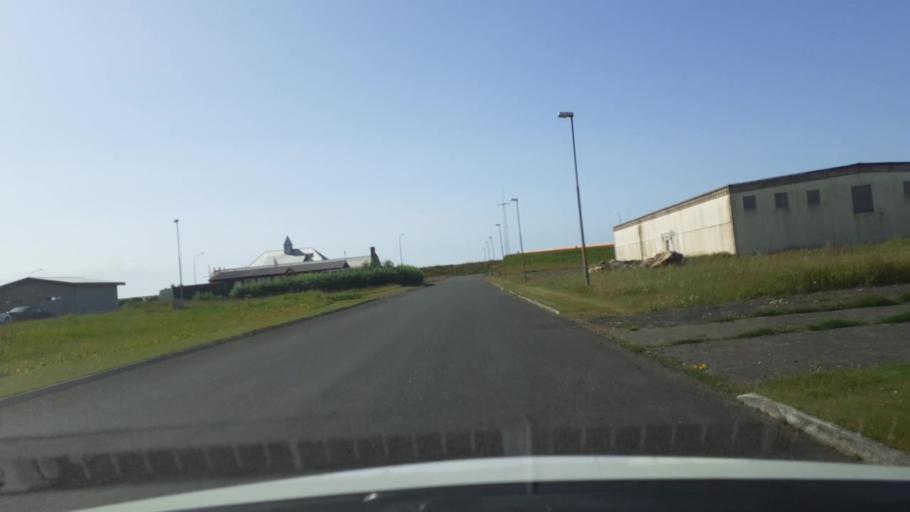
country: IS
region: South
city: Hveragerdi
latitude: 63.8667
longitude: -21.1593
